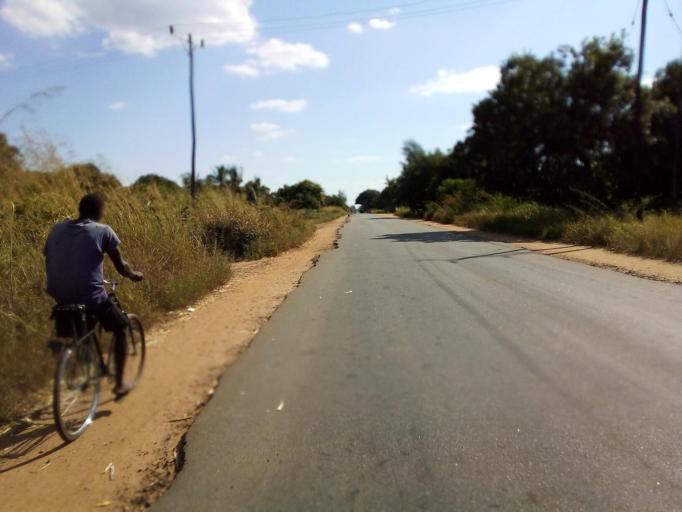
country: MZ
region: Zambezia
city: Quelimane
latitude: -17.5769
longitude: 36.6581
